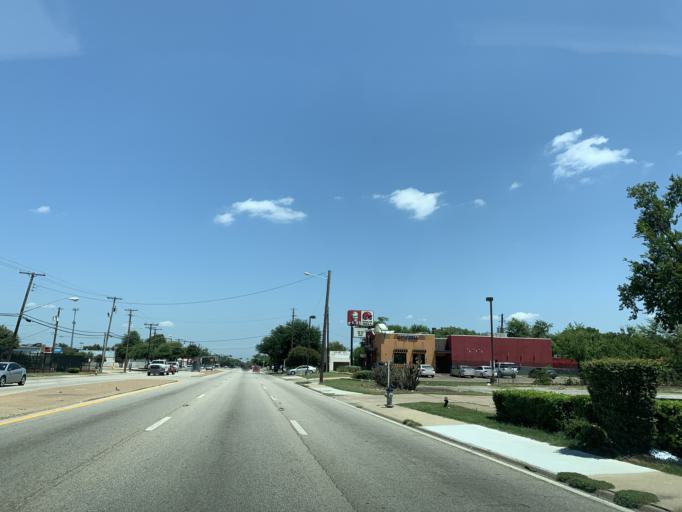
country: US
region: Texas
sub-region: Dallas County
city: Hutchins
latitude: 32.6930
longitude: -96.7750
